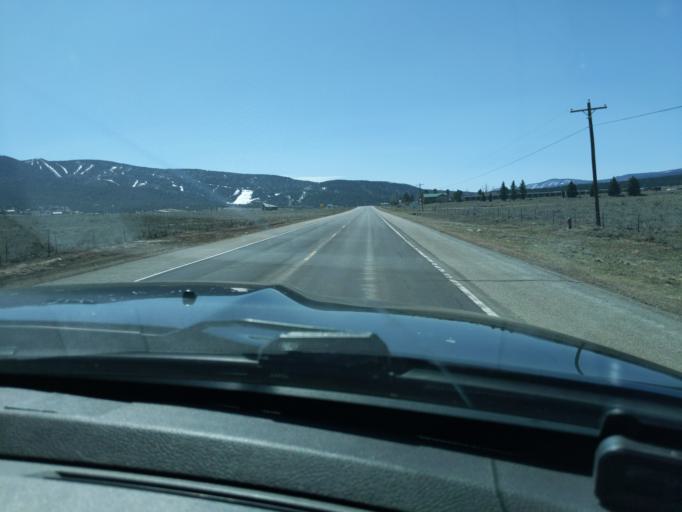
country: US
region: New Mexico
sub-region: Colfax County
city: Angel Fire
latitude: 36.4158
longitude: -105.2948
